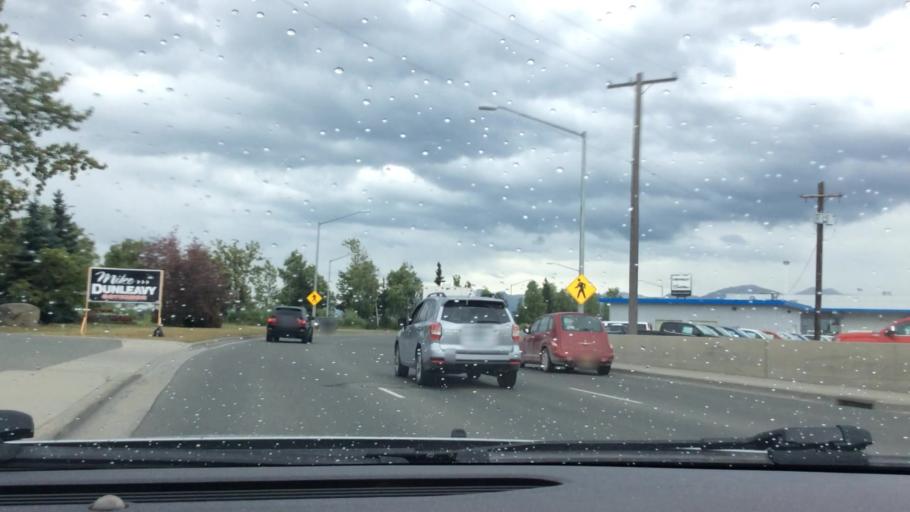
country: US
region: Alaska
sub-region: Anchorage Municipality
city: Anchorage
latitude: 61.2170
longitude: -149.8609
